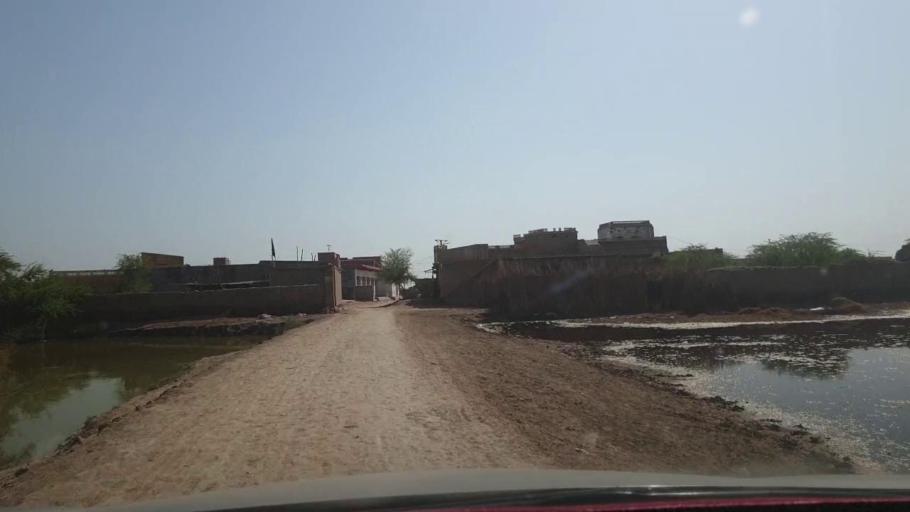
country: PK
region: Sindh
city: Nasirabad
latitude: 27.3462
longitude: 67.8409
